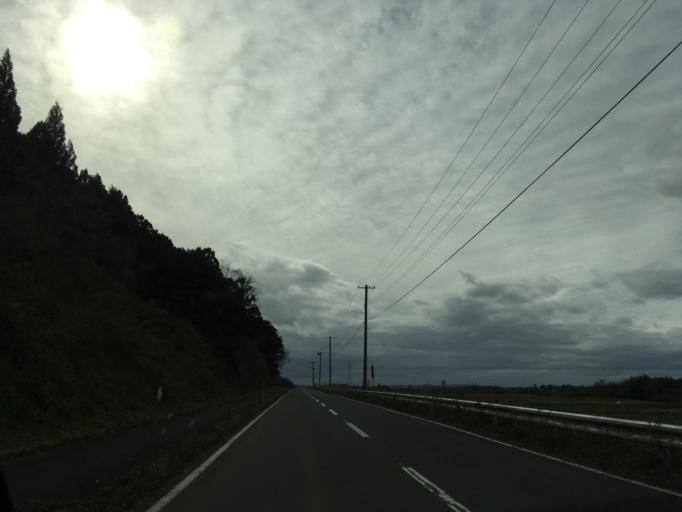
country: JP
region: Iwate
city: Ichinoseki
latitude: 38.7410
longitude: 141.2794
